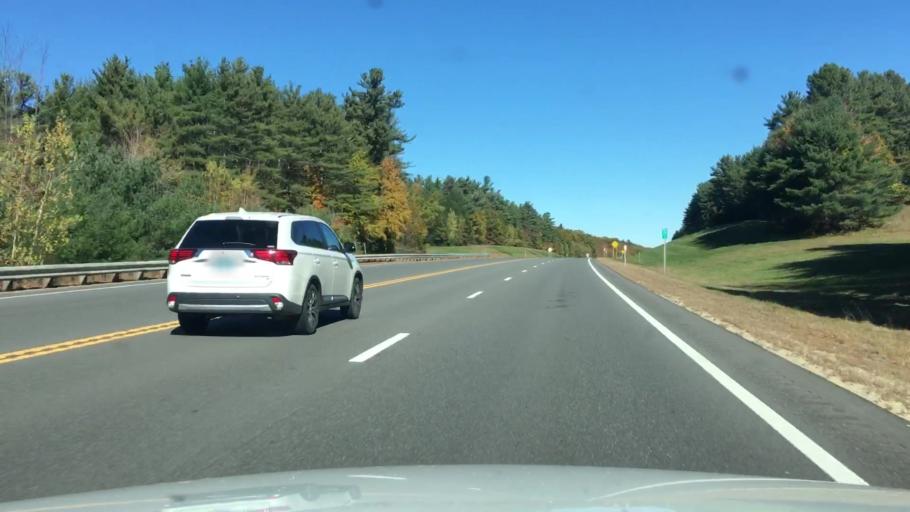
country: US
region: New Hampshire
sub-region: Strafford County
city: Farmington
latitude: 43.4270
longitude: -71.0096
